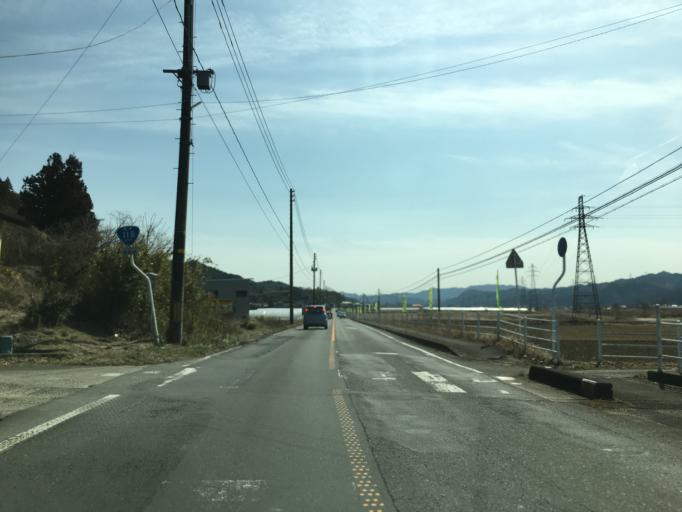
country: JP
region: Ibaraki
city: Daigo
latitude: 36.9239
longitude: 140.4153
